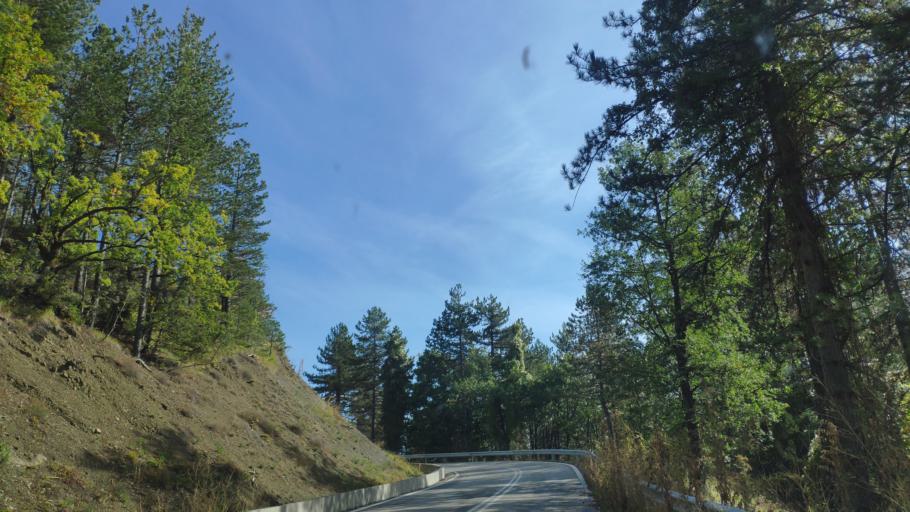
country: AL
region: Korce
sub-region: Rrethi i Devollit
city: Miras
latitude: 40.3726
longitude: 20.9224
